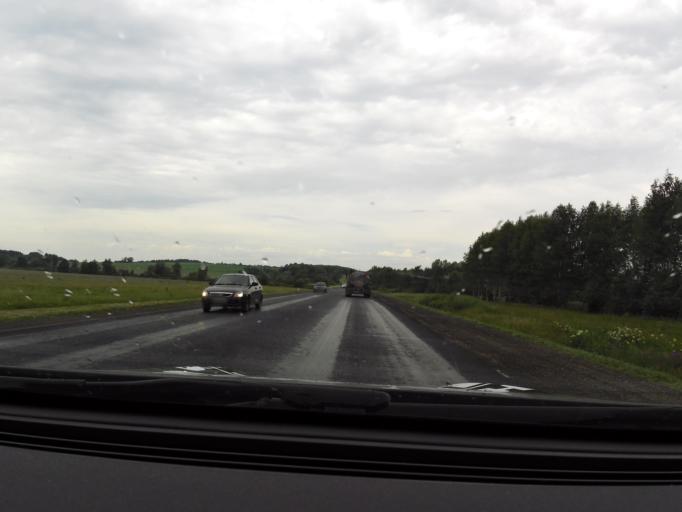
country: RU
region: Bashkortostan
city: Iglino
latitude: 54.7757
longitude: 56.4821
